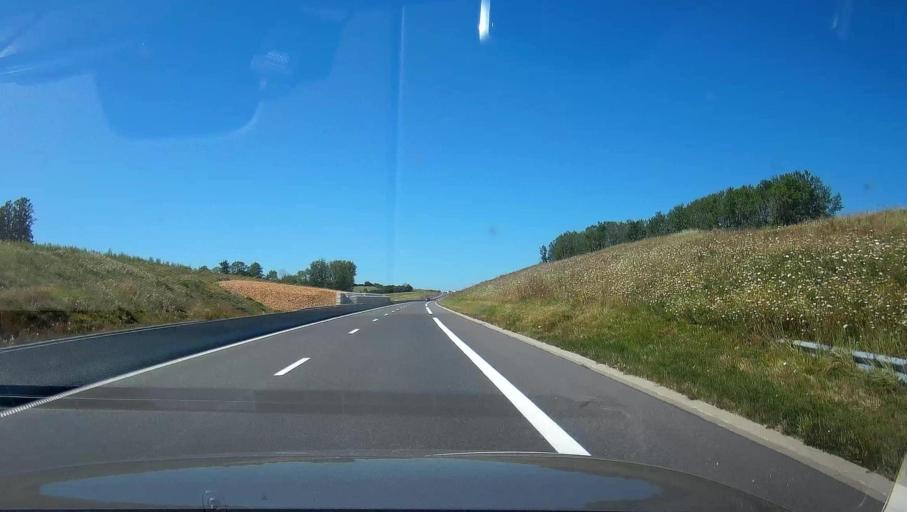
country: FR
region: Champagne-Ardenne
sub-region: Departement des Ardennes
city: Tournes
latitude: 49.7735
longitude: 4.6250
